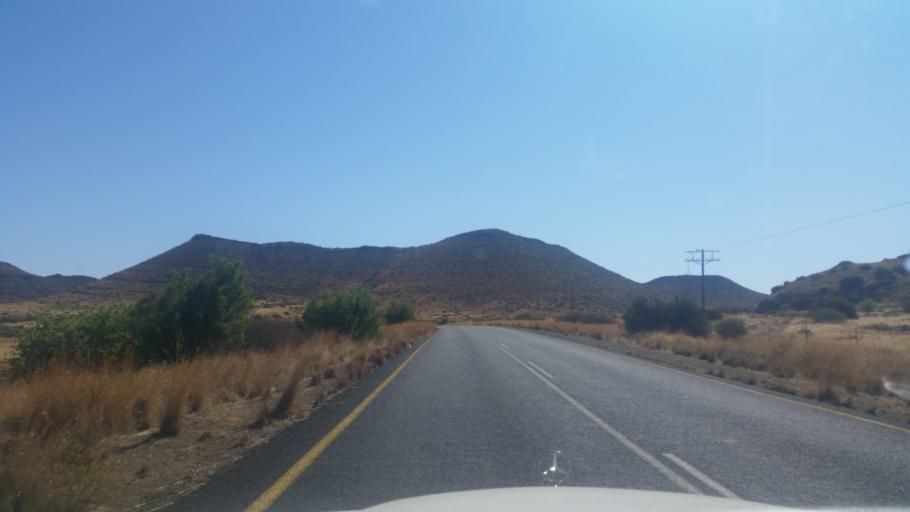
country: ZA
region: Orange Free State
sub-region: Xhariep District Municipality
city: Trompsburg
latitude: -30.4832
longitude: 25.9979
